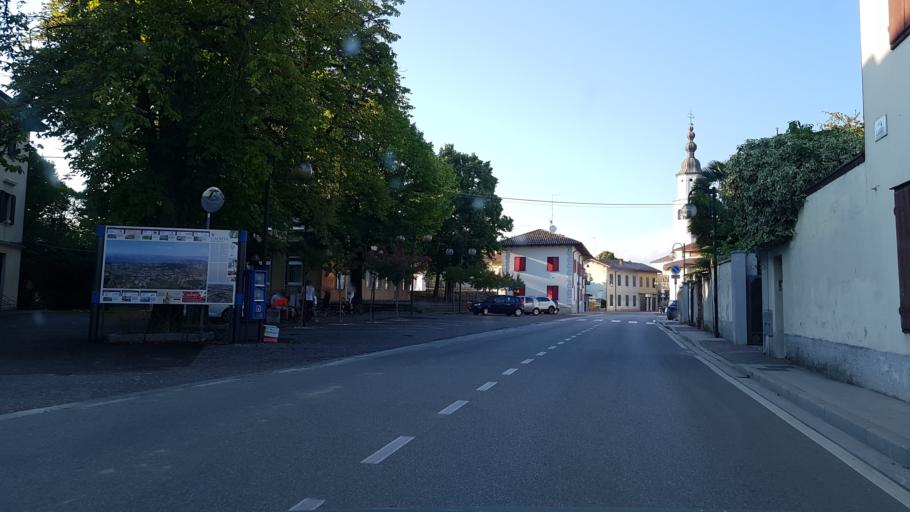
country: IT
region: Friuli Venezia Giulia
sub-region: Provincia di Gorizia
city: Capriva del Friuli
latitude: 45.9411
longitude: 13.5143
